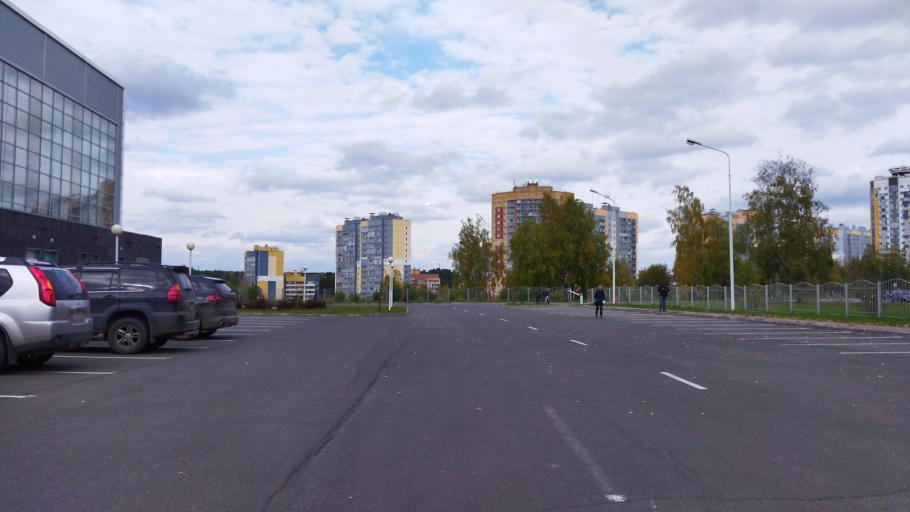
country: RU
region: Tomsk
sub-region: Tomskiy Rayon
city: Tomsk
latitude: 56.4937
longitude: 85.0594
